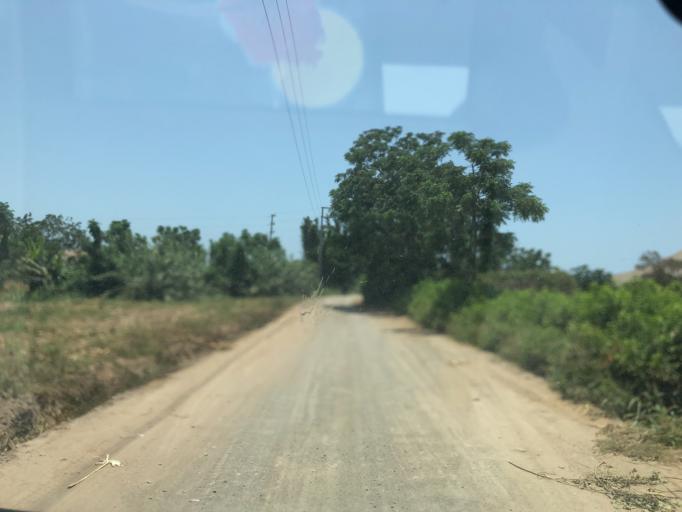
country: PE
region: Lima
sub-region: Provincia de Canete
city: Quilmana
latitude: -13.0025
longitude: -76.4494
